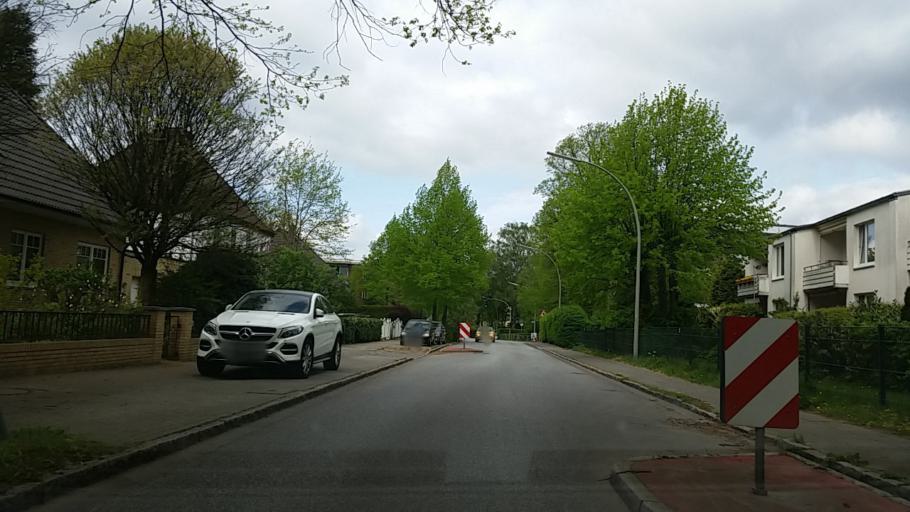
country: DE
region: Hamburg
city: Harburg
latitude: 53.4387
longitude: 10.0027
